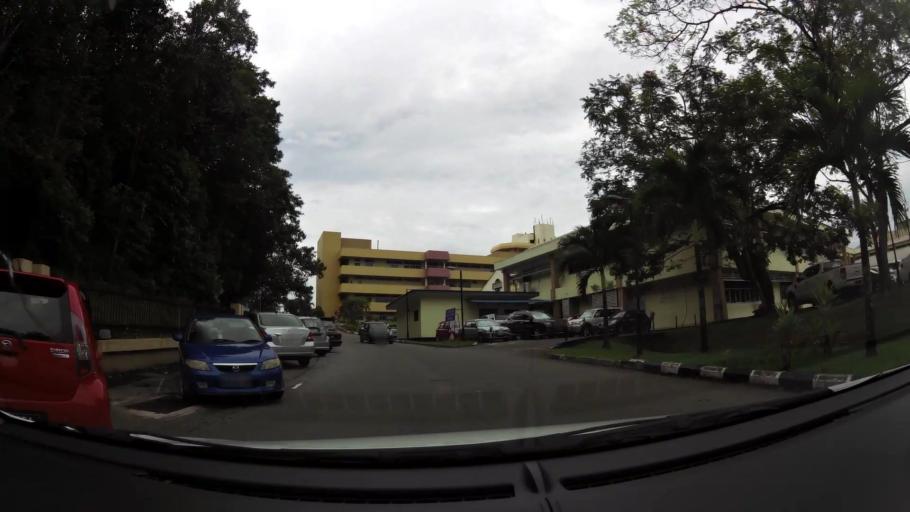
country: BN
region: Brunei and Muara
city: Bandar Seri Begawan
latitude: 4.8929
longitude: 114.9328
